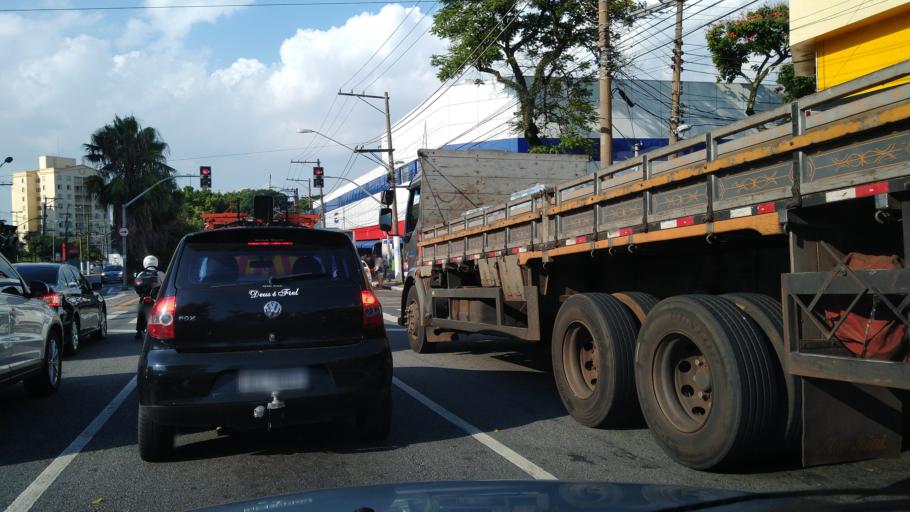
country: BR
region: Sao Paulo
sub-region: Sao Paulo
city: Sao Paulo
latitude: -23.5547
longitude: -46.5999
